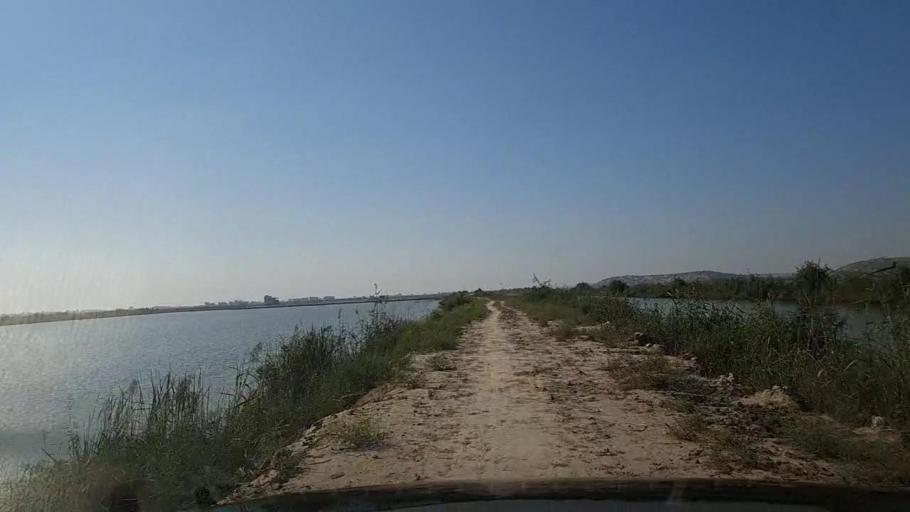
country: PK
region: Sindh
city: Thatta
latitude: 24.6883
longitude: 67.8931
